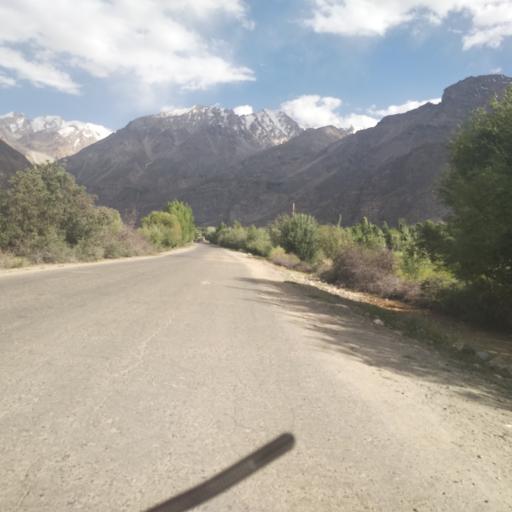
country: TJ
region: Gorno-Badakhshan
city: Roshtqal'a
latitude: 37.7273
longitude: 72.1599
